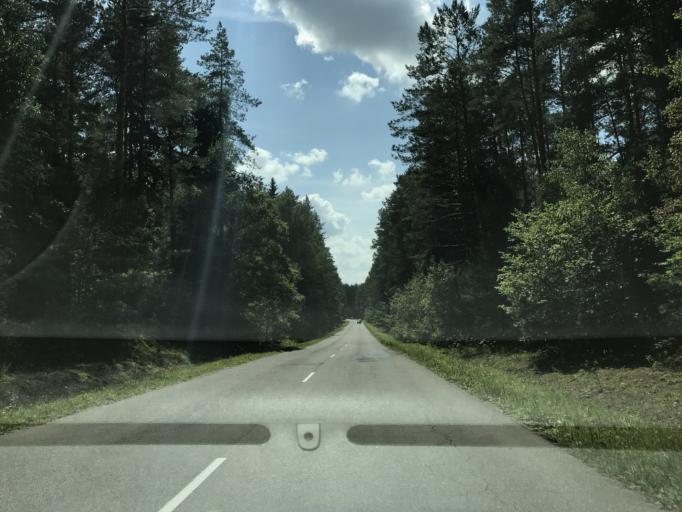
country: BY
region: Minsk
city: Rakaw
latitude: 53.9899
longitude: 26.9909
